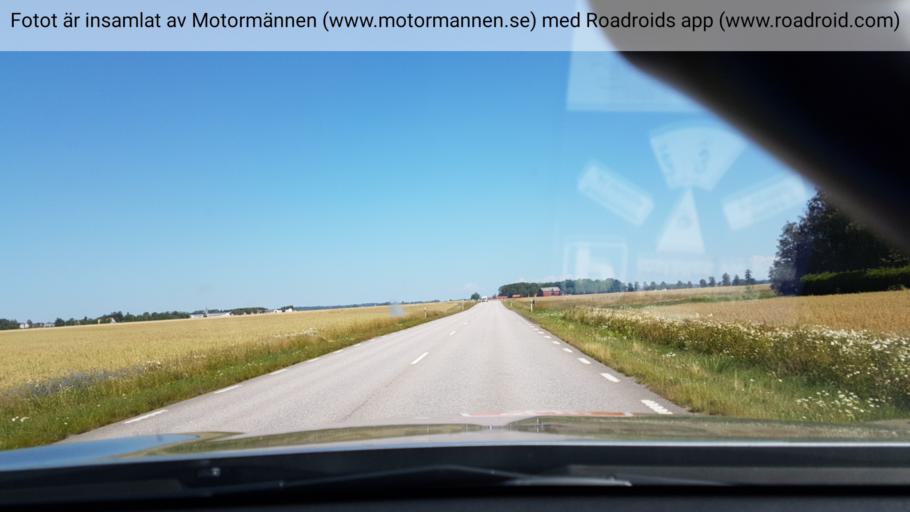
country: SE
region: Vaestra Goetaland
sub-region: Lidkopings Kommun
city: Lidkoping
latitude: 58.4274
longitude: 13.0437
